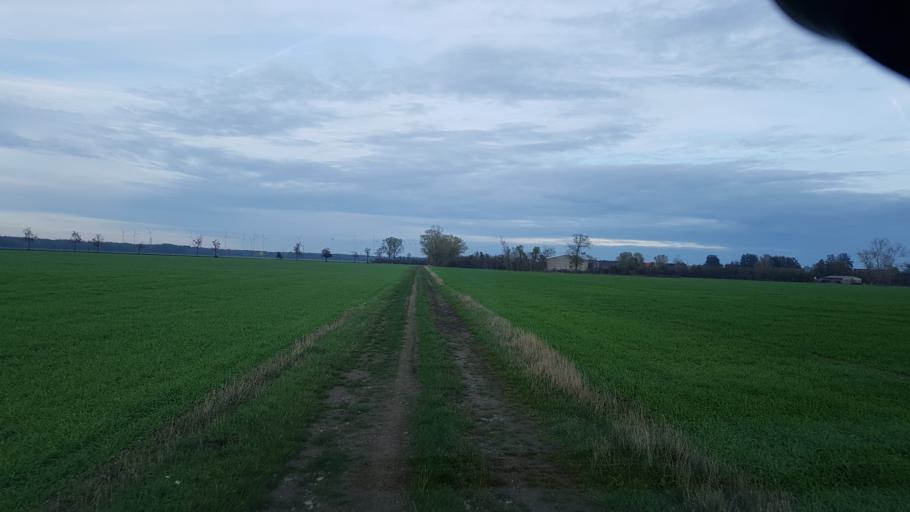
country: DE
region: Brandenburg
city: Falkenberg
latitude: 51.5395
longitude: 13.2726
